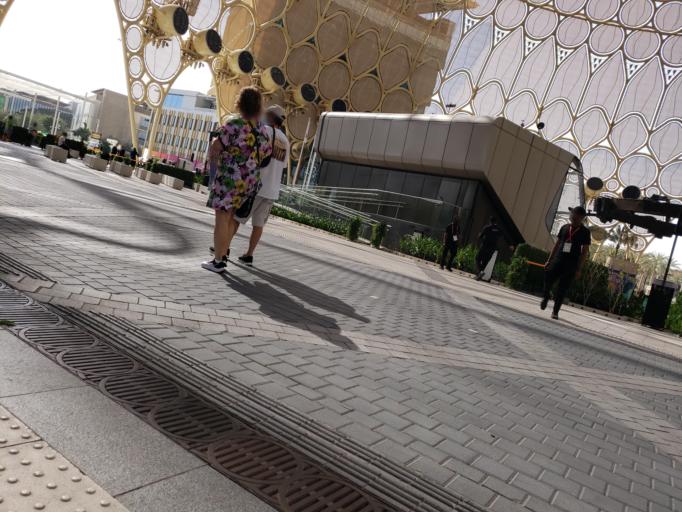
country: AE
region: Dubai
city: Dubai
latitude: 24.9614
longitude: 55.1507
